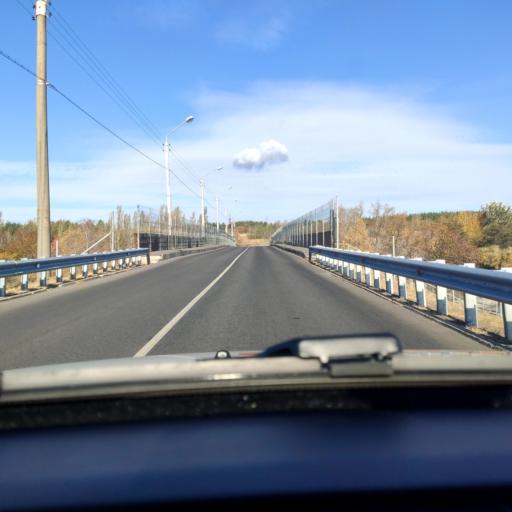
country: RU
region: Voronezj
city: Shilovo
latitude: 51.5495
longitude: 39.1353
